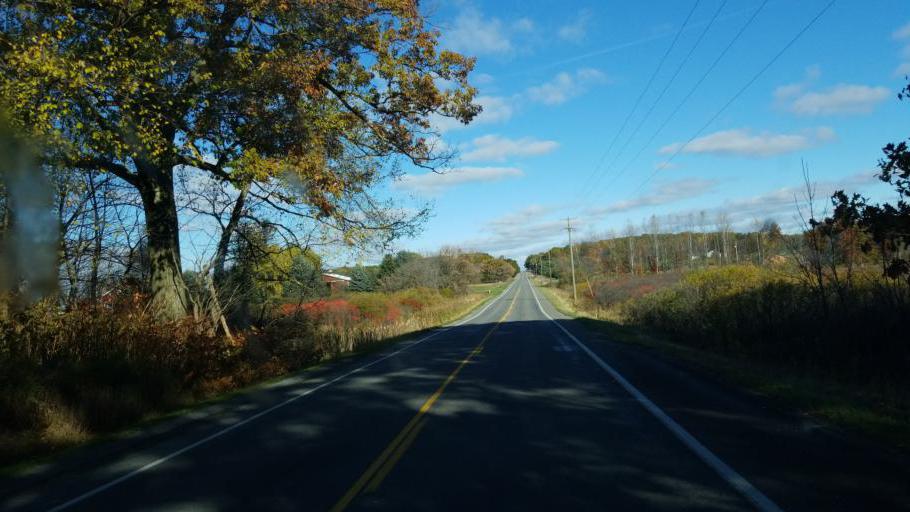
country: US
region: Michigan
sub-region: Montcalm County
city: Edmore
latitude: 43.4299
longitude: -85.0442
